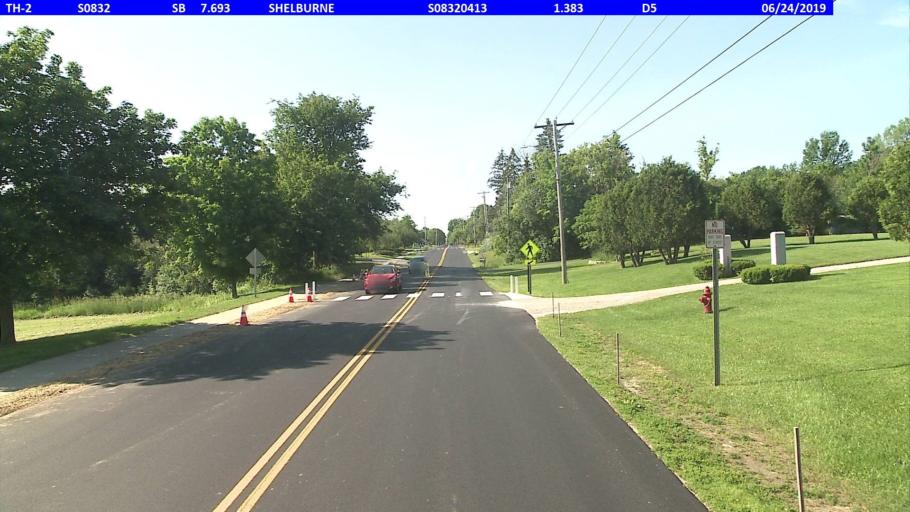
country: US
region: Vermont
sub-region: Chittenden County
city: Burlington
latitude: 44.3746
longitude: -73.2257
